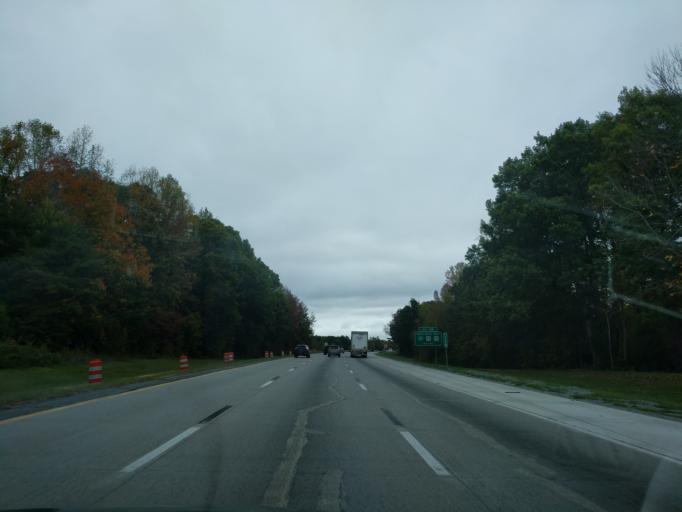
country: US
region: North Carolina
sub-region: Guilford County
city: Jamestown
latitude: 35.9820
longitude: -79.8868
